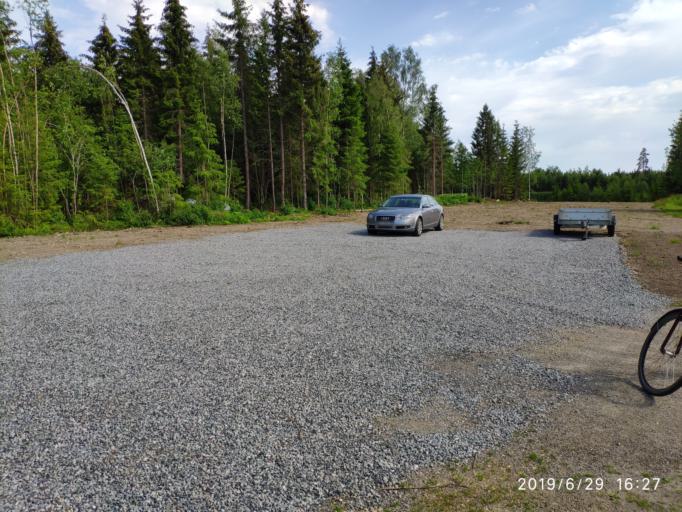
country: NO
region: Akershus
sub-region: Ullensaker
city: Jessheim
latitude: 60.1666
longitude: 11.1740
